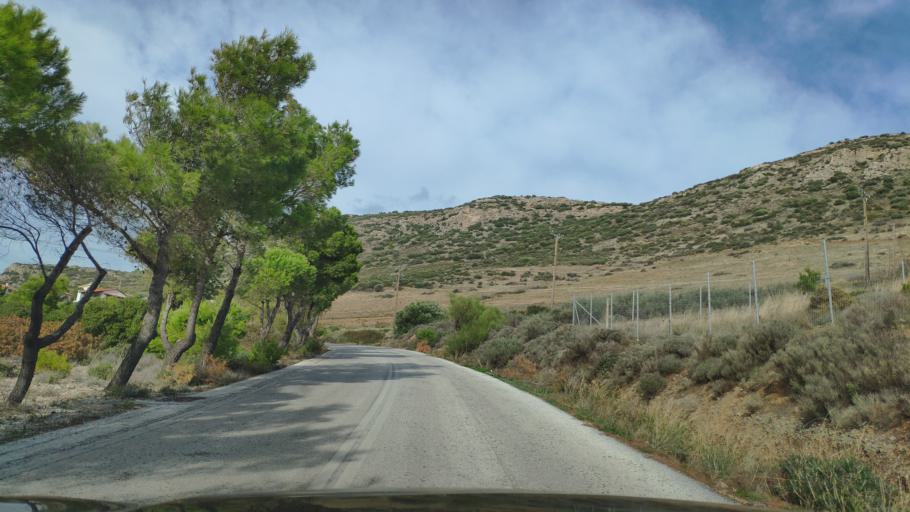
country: GR
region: Attica
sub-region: Nomarchia Anatolikis Attikis
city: Limin Mesoyaias
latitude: 37.9042
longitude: 24.0241
